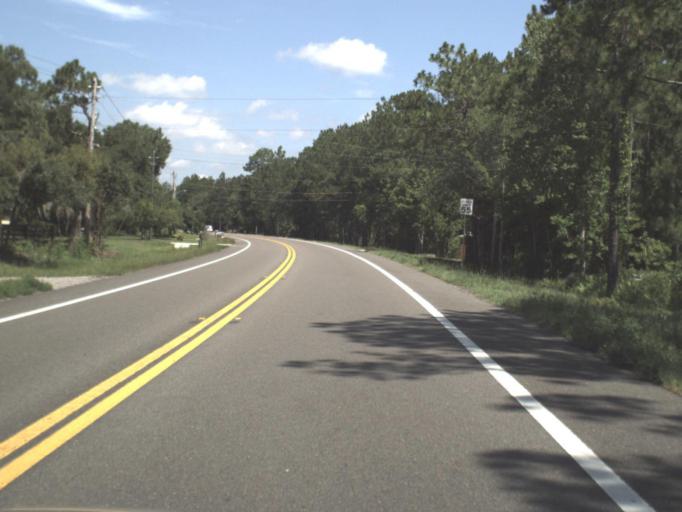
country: US
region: Florida
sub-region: Clay County
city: Green Cove Springs
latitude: 29.9726
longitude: -81.5395
